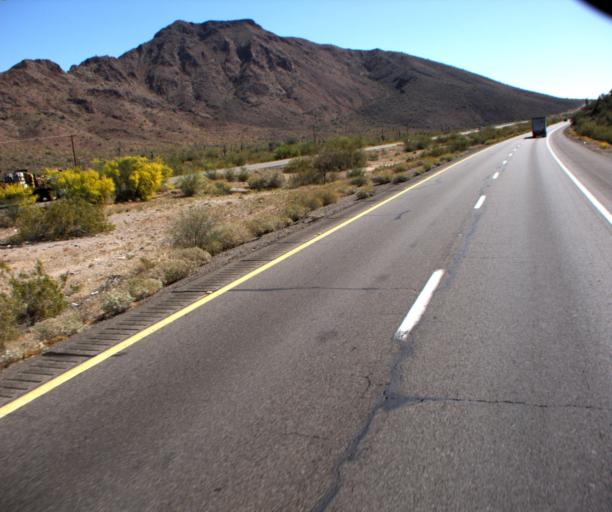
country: US
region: Arizona
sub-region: La Paz County
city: Quartzsite
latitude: 33.6774
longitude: -114.0600
